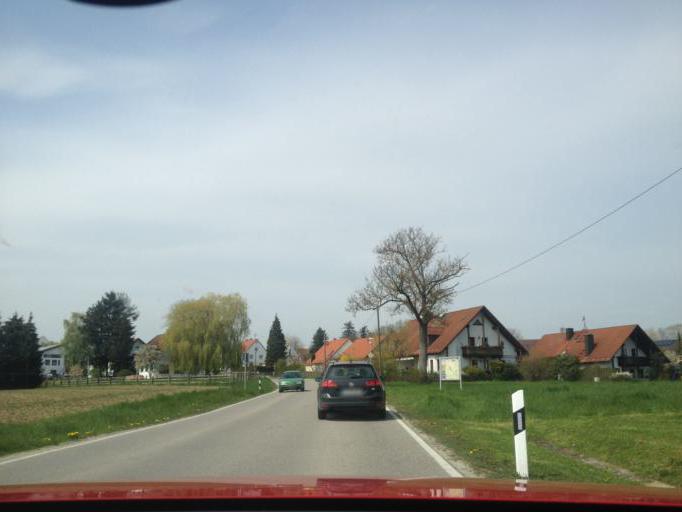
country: DE
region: Bavaria
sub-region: Upper Bavaria
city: Paunzhausen
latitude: 48.4735
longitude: 11.5713
